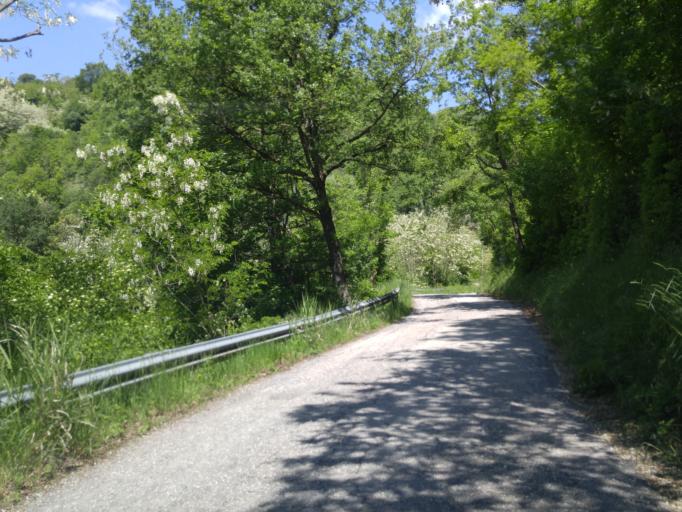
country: IT
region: The Marches
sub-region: Provincia di Pesaro e Urbino
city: Fermignano
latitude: 43.7137
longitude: 12.6754
